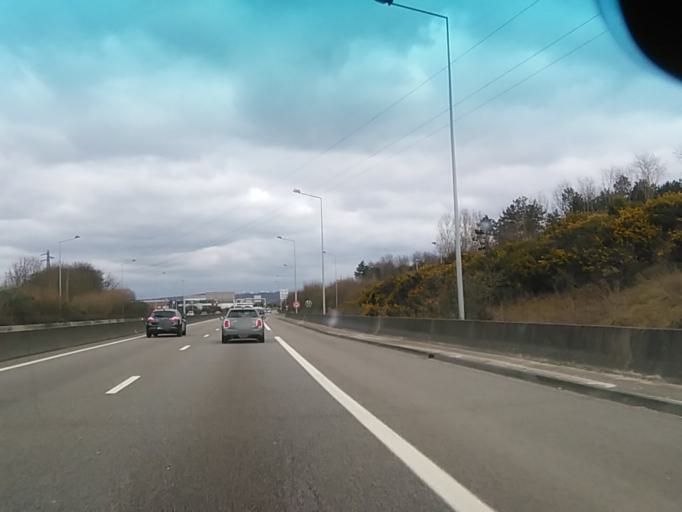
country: FR
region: Haute-Normandie
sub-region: Departement de la Seine-Maritime
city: Le Grand-Quevilly
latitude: 49.4010
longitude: 1.0325
